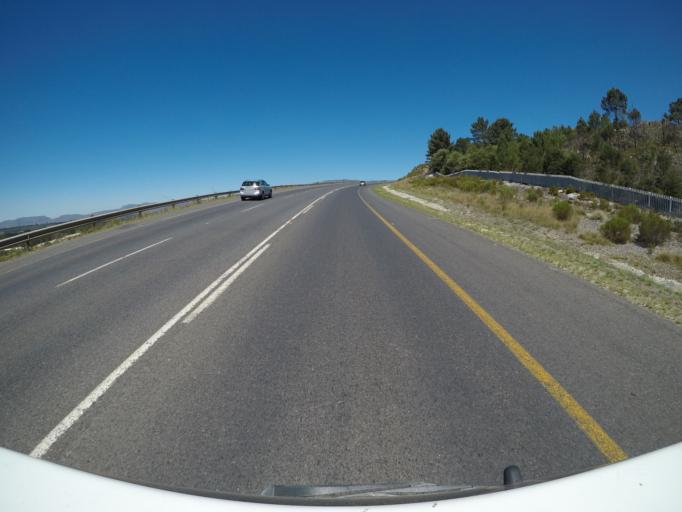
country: ZA
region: Western Cape
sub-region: Overberg District Municipality
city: Grabouw
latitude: -34.1660
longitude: 19.0020
